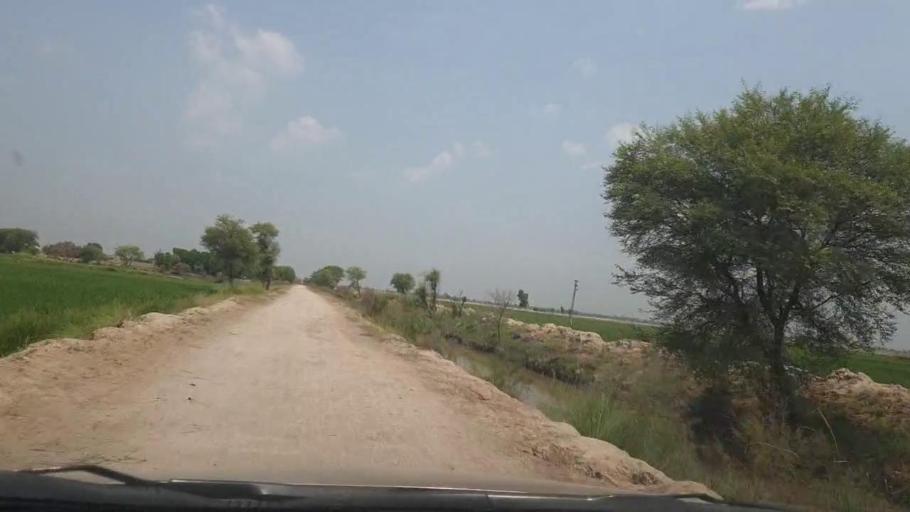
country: PK
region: Sindh
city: Ratodero
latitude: 27.6946
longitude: 68.2331
